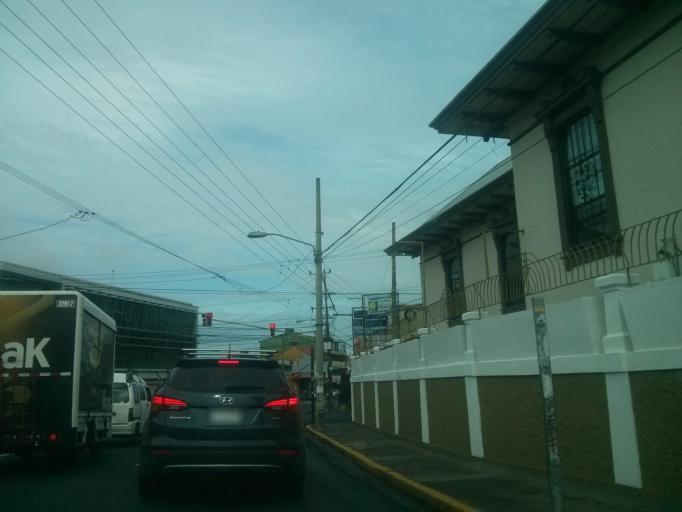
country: CR
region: San Jose
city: San Jose
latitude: 9.9323
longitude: -84.0676
